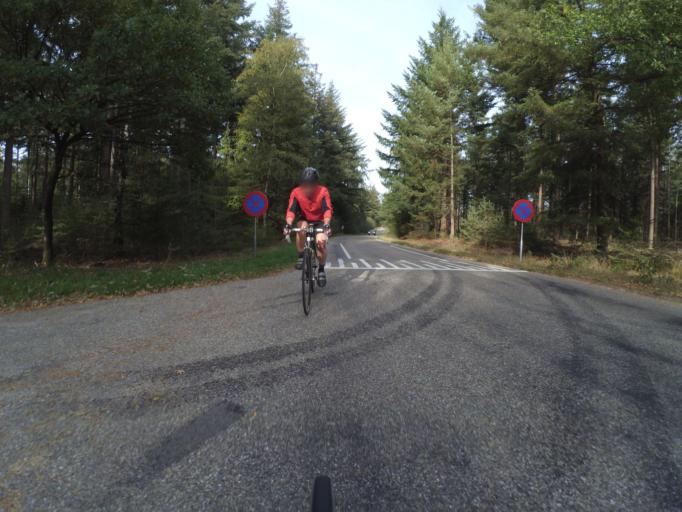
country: NL
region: Overijssel
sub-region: Gemeente Hof van Twente
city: Markelo
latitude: 52.3157
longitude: 6.4143
